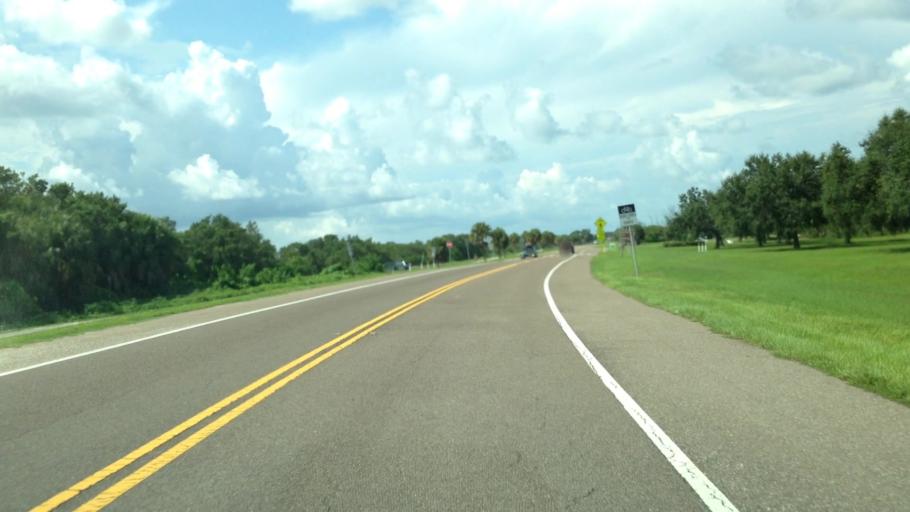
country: US
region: Florida
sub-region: Pinellas County
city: Tierra Verde
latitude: 27.6479
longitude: -82.7111
